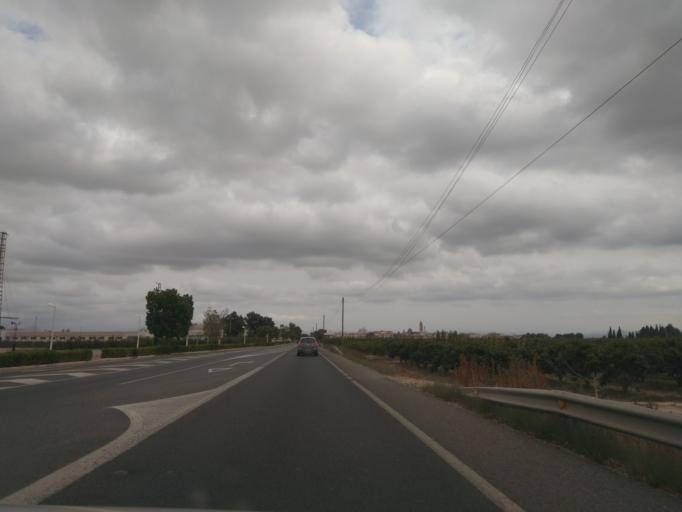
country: ES
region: Valencia
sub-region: Provincia de Valencia
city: L'Alcudia
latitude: 39.2088
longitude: -0.5107
